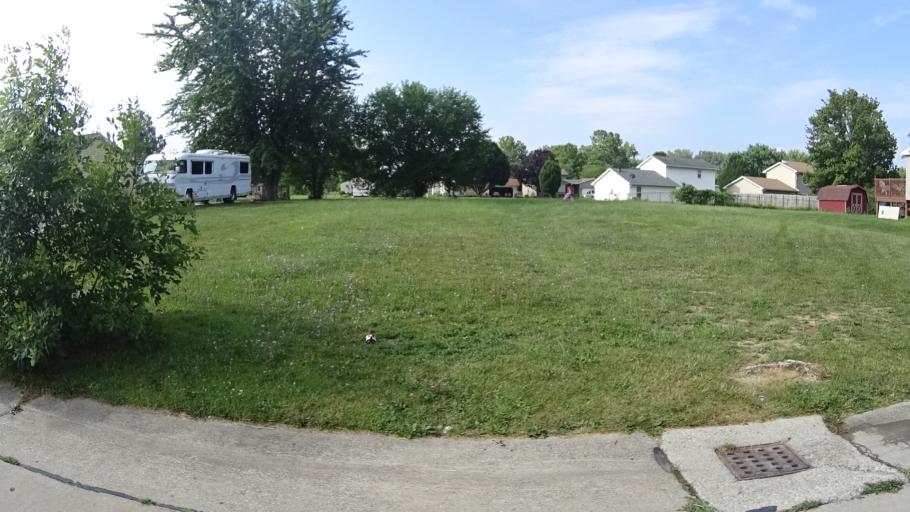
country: US
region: Ohio
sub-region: Erie County
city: Sandusky
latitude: 41.4352
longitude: -82.6704
